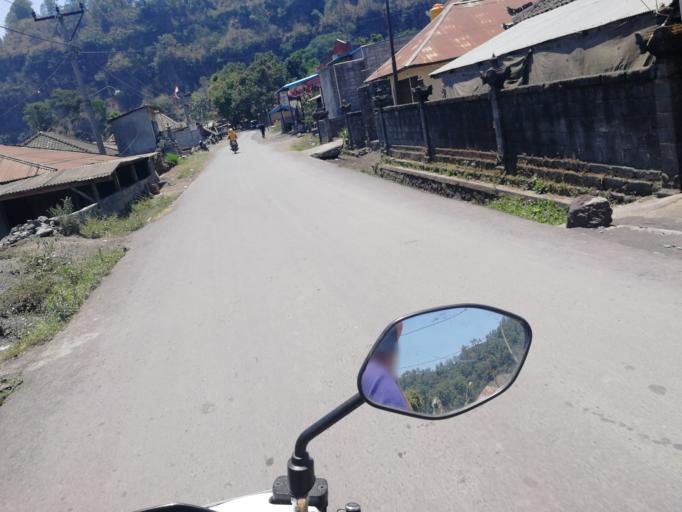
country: ID
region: Bali
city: Banjar Trunyan
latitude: -8.2231
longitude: 115.4121
